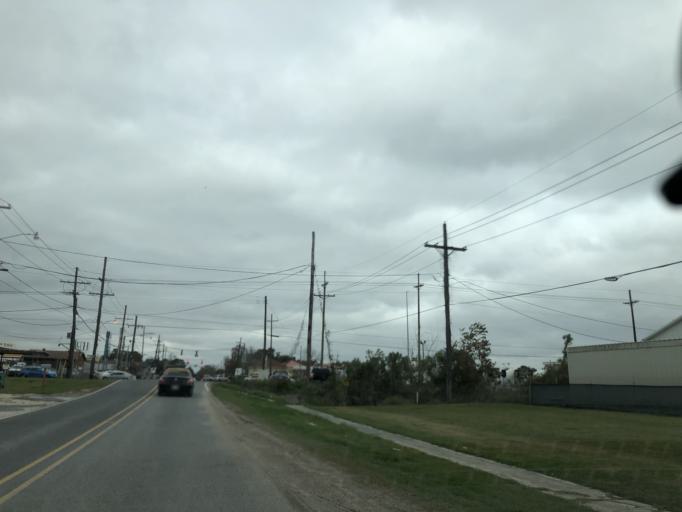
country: US
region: Louisiana
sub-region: Jefferson Parish
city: Metairie Terrace
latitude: 29.9738
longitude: -90.1607
